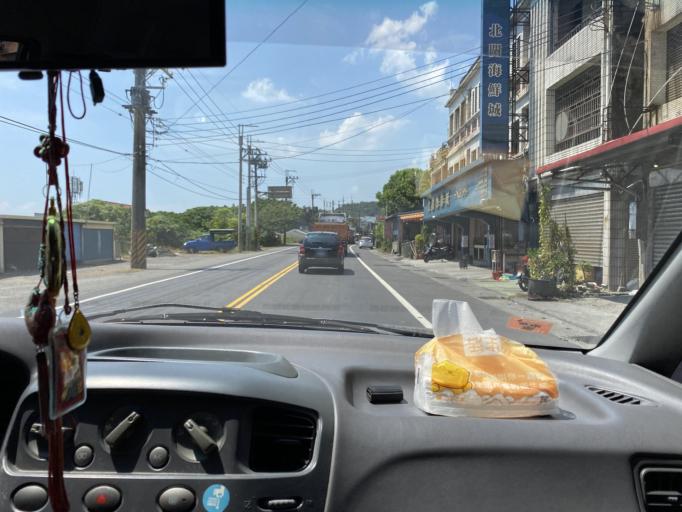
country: TW
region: Taiwan
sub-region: Yilan
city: Yilan
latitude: 24.9053
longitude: 121.8699
